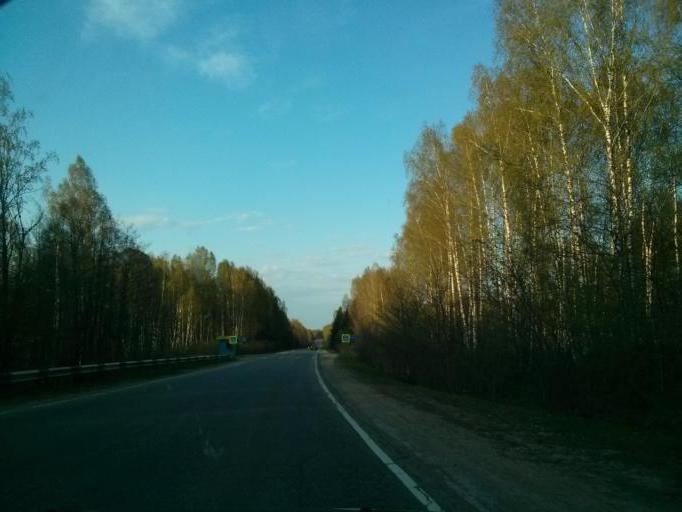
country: RU
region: Nizjnij Novgorod
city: Navashino
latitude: 55.7306
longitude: 42.3731
